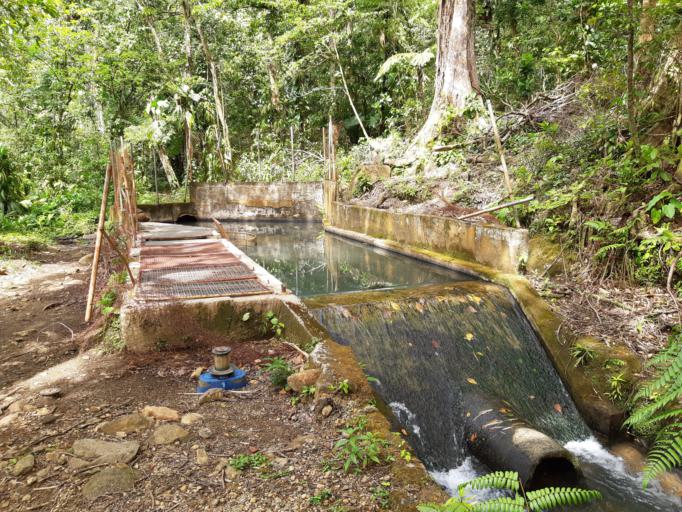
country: GP
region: Guadeloupe
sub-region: Guadeloupe
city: Saint-Claude
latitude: 16.0323
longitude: -61.6788
